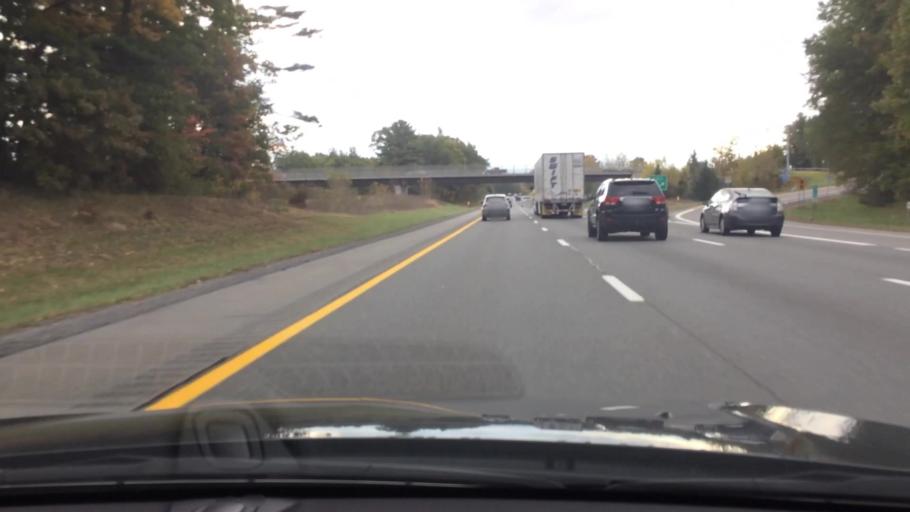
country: US
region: New York
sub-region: Saratoga County
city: Country Knolls
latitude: 42.9038
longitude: -73.7874
